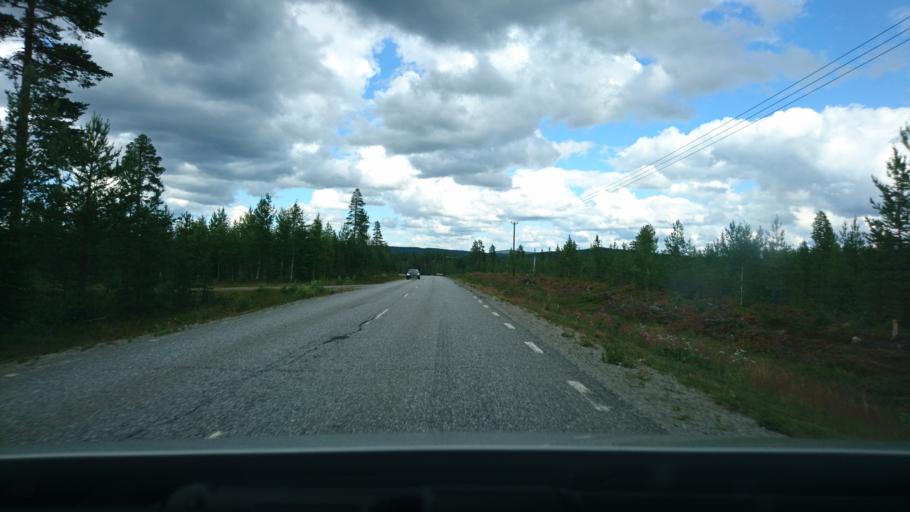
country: SE
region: Vaesterbotten
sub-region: Asele Kommun
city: Asele
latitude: 63.9164
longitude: 17.2378
